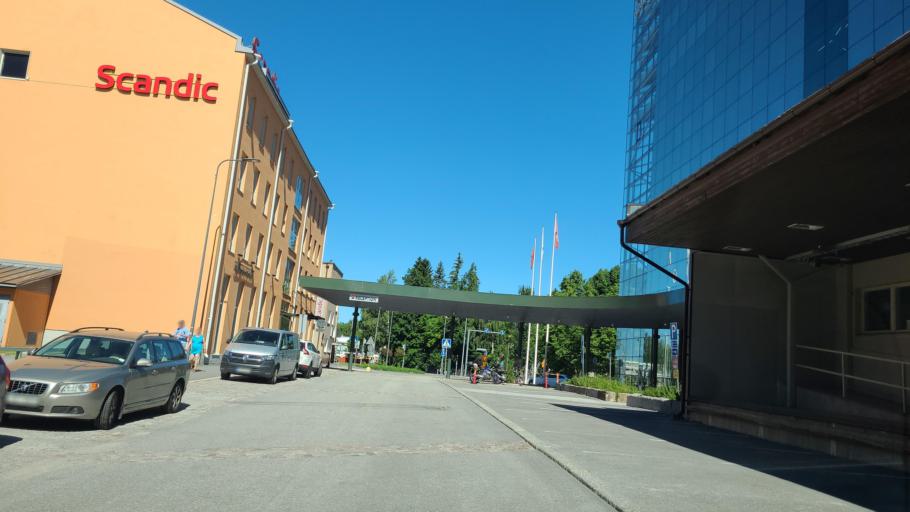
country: FI
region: Ostrobothnia
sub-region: Vaasa
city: Vaasa
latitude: 63.0977
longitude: 21.6195
